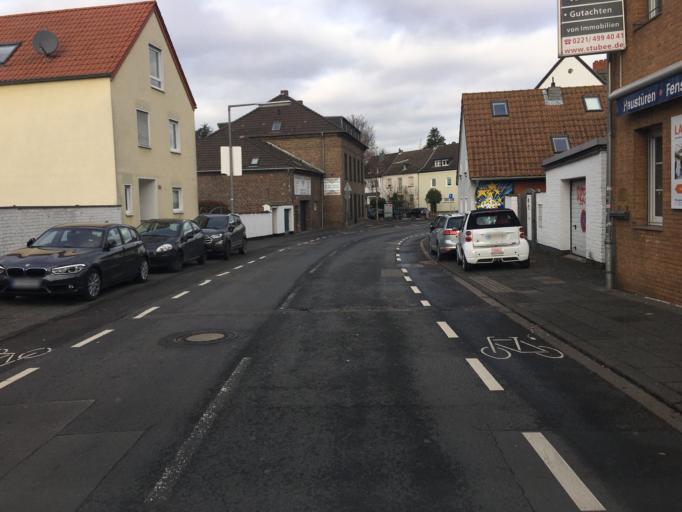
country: DE
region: North Rhine-Westphalia
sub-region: Regierungsbezirk Koln
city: Mengenich
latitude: 50.9415
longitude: 6.8793
